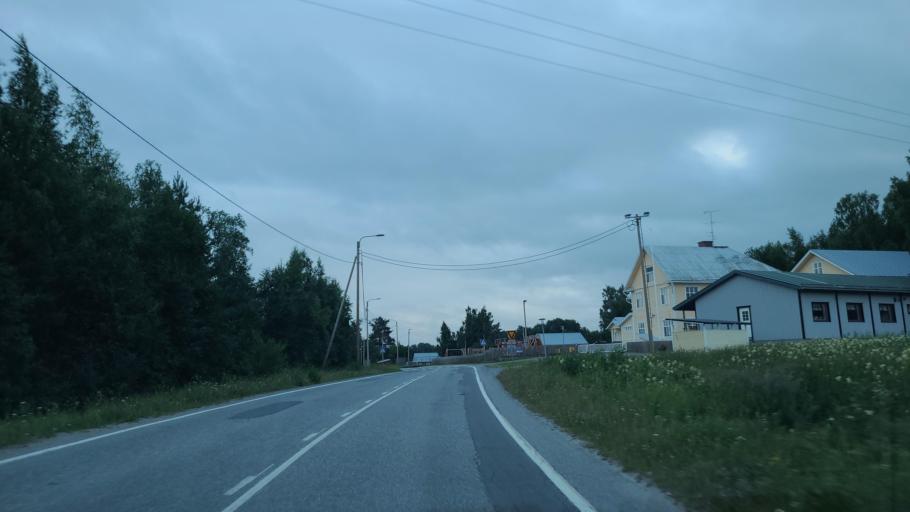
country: FI
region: Ostrobothnia
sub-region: Vaasa
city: Replot
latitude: 63.1983
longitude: 21.3040
